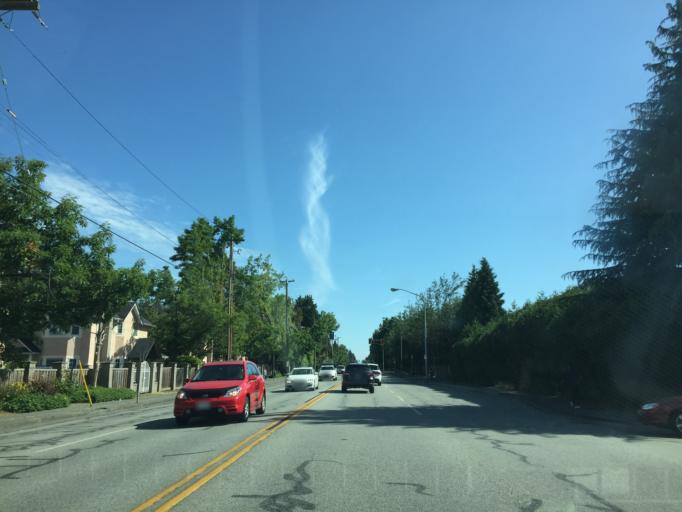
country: CA
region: British Columbia
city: Richmond
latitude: 49.1604
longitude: -123.1366
